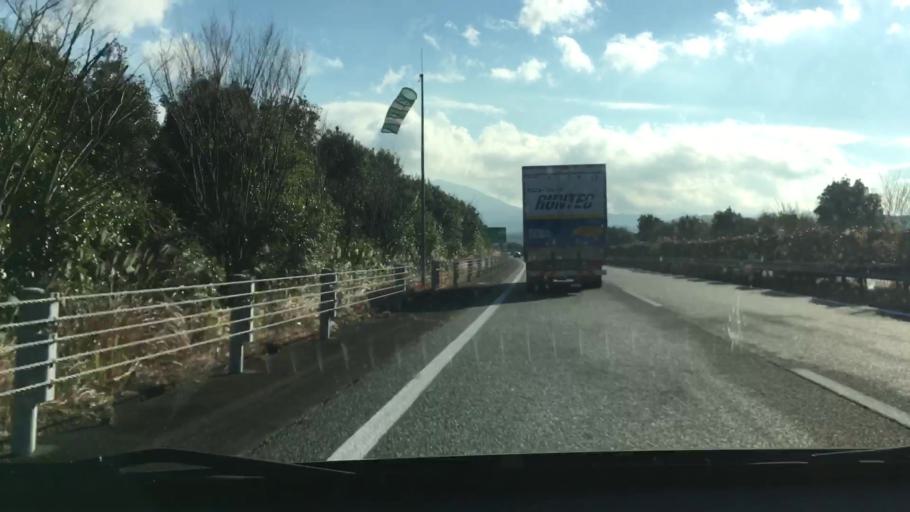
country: JP
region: Kumamoto
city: Hitoyoshi
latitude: 32.0586
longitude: 130.8031
